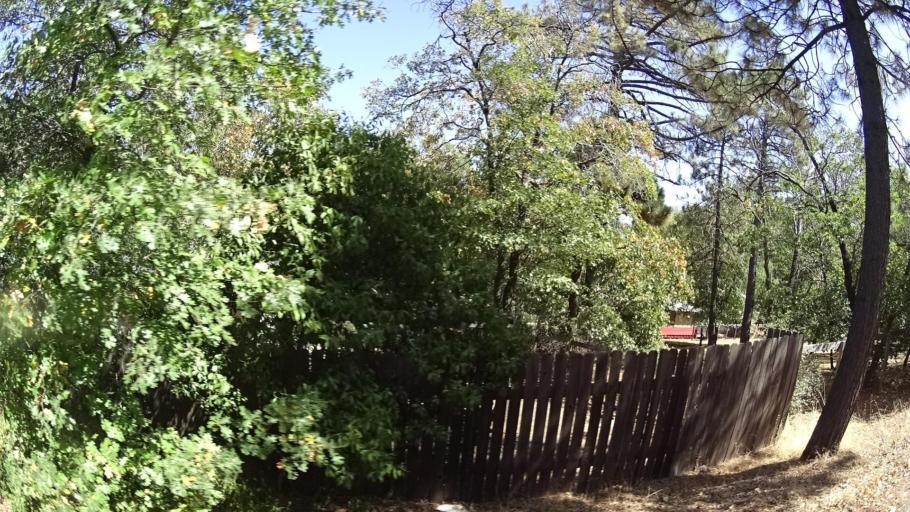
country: US
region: California
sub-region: San Diego County
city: Julian
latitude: 33.0710
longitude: -116.5762
